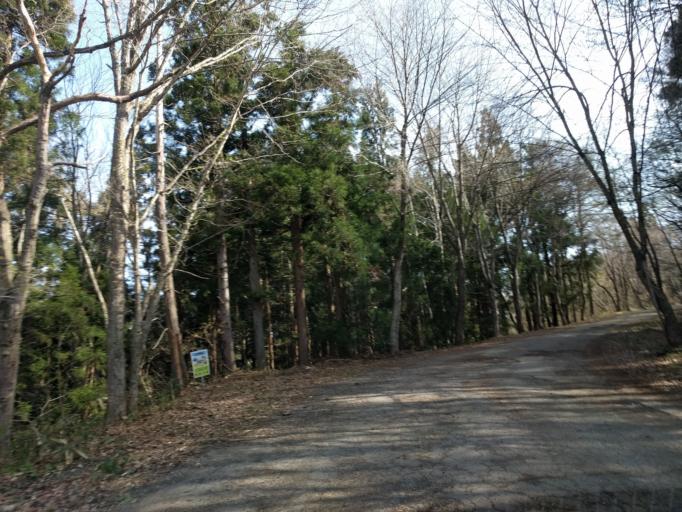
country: JP
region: Fukushima
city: Inawashiro
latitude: 37.5221
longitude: 140.0323
